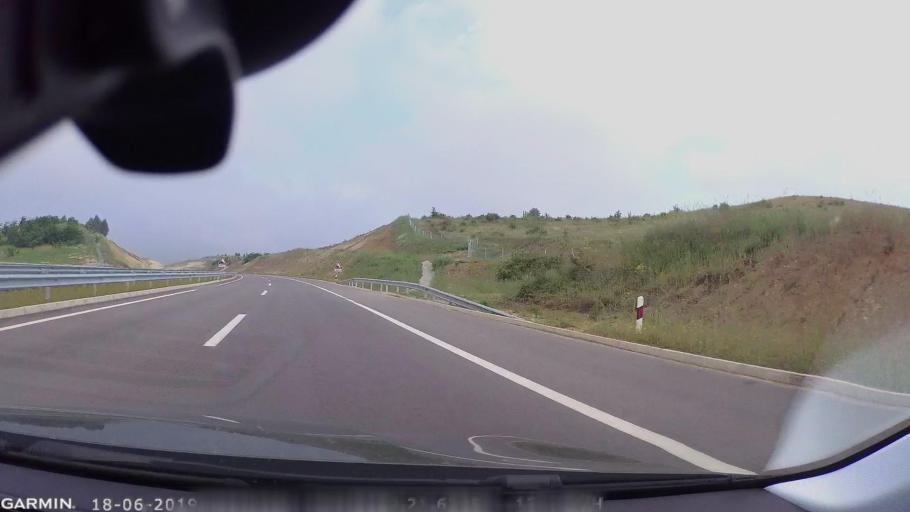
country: MK
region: Petrovec
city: Sredno Konjare
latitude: 41.9470
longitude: 21.7798
